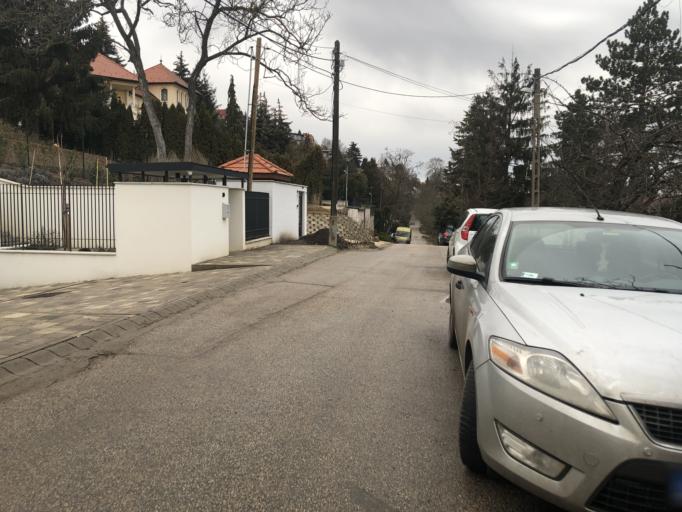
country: HU
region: Pest
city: Budakeszi
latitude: 47.5464
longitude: 18.9470
